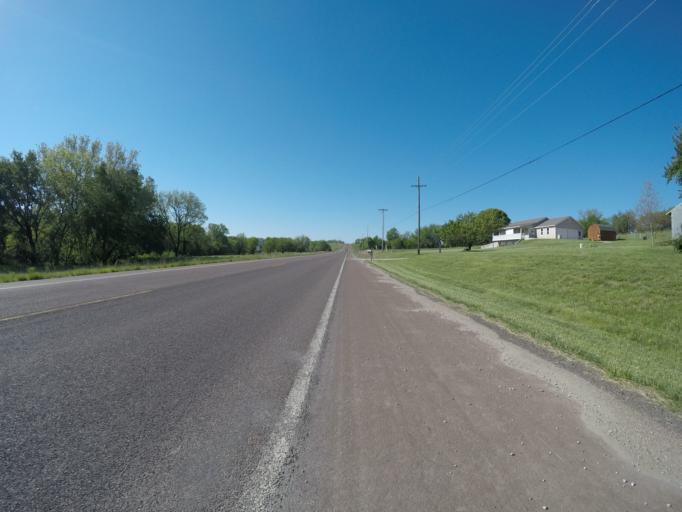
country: US
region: Kansas
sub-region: Douglas County
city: Lawrence
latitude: 39.0376
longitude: -95.3913
